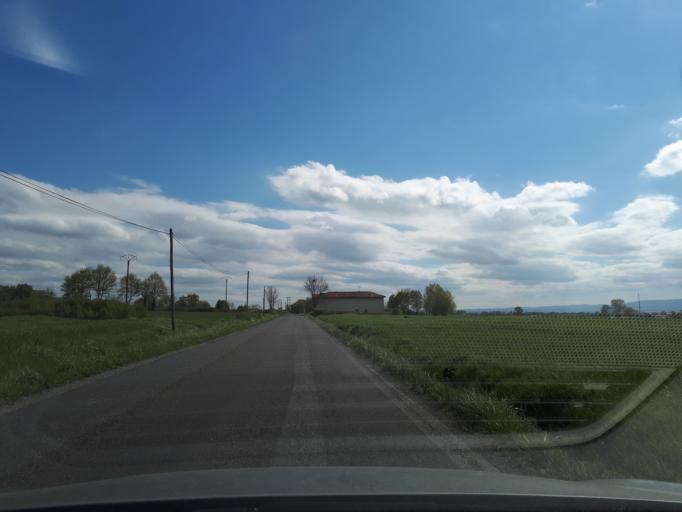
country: FR
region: Rhone-Alpes
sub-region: Departement de la Loire
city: Bellegarde-en-Forez
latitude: 45.6670
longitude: 4.2928
